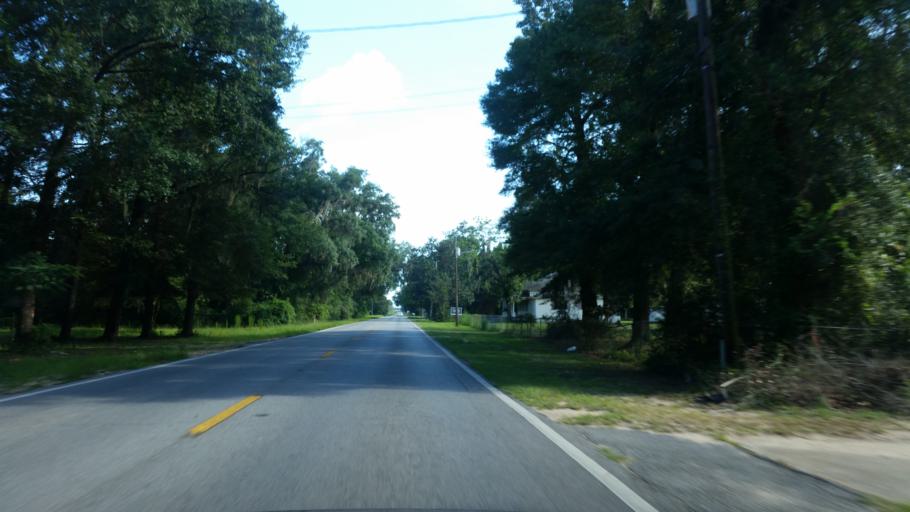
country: US
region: Florida
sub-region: Santa Rosa County
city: Bagdad
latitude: 30.5919
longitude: -87.0310
